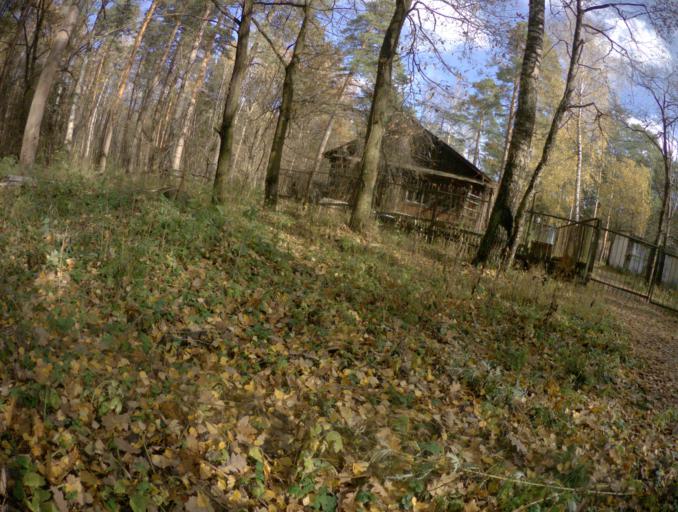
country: RU
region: Vladimir
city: Kommunar
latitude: 56.0724
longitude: 40.4446
